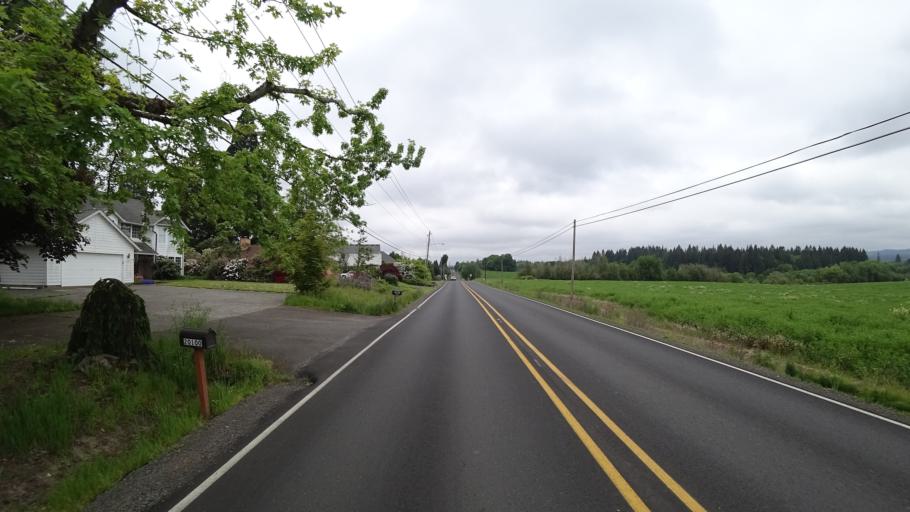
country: US
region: Oregon
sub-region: Washington County
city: Rockcreek
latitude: 45.5608
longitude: -122.8843
